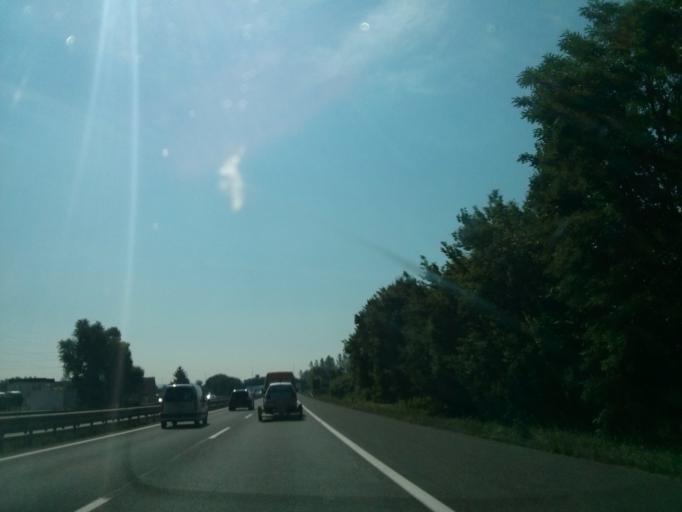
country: SI
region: Ljubljana
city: Ljubljana
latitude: 46.0330
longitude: 14.4698
